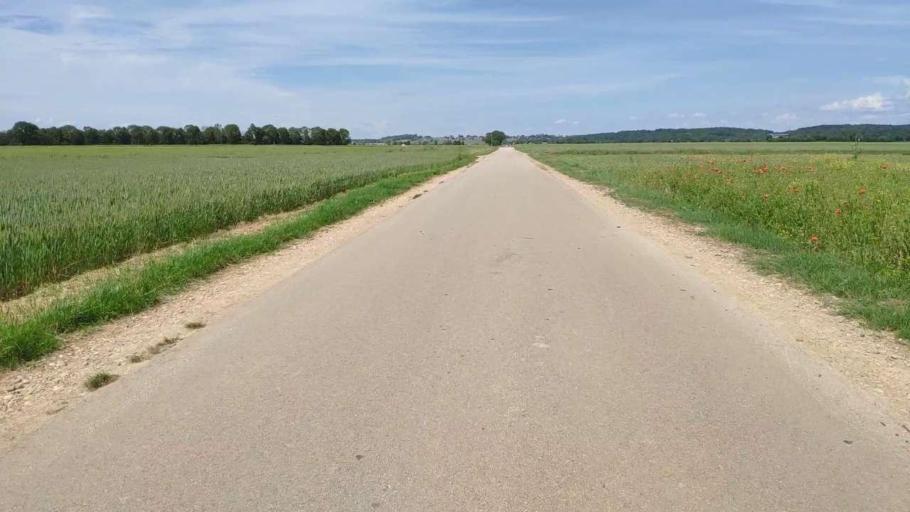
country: FR
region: Franche-Comte
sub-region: Departement du Jura
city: Bletterans
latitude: 46.7503
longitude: 5.4944
